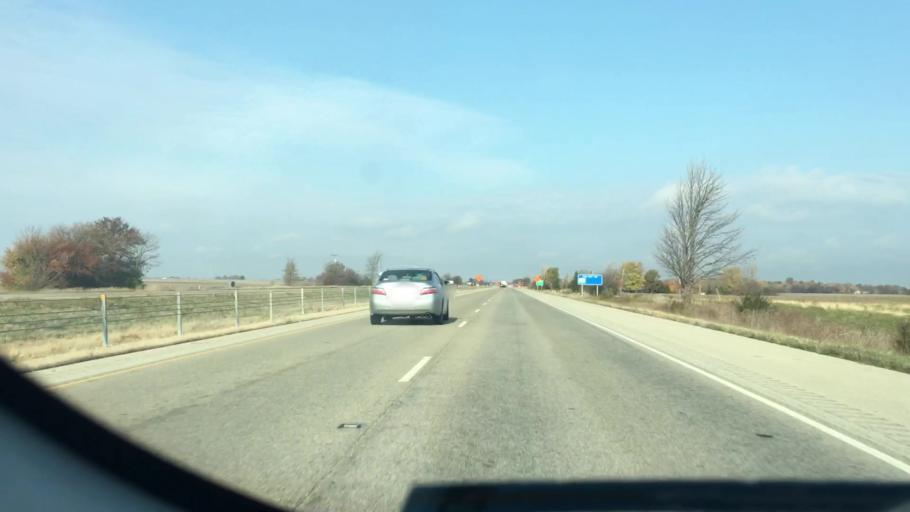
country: US
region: Illinois
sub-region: McLean County
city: Danvers
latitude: 40.5666
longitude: -89.1191
